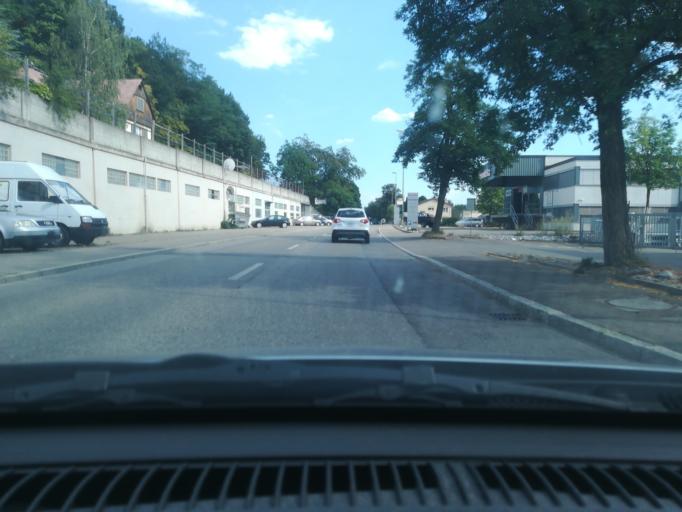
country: CH
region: Schaffhausen
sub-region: Bezirk Schaffhausen
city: Schaffhausen
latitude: 47.7220
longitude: 8.6436
